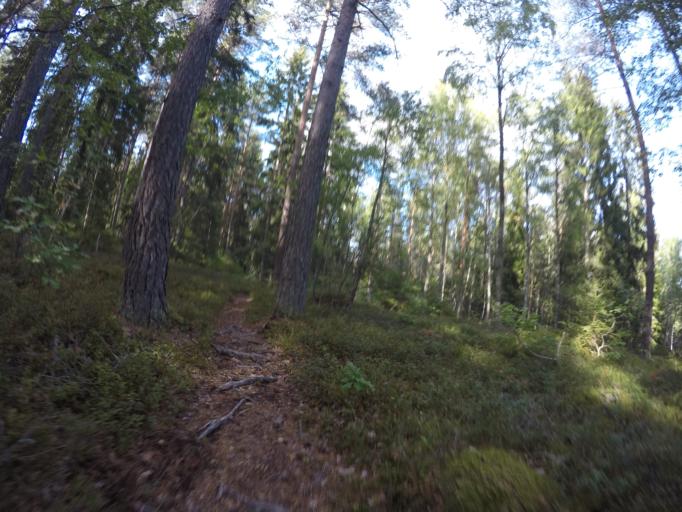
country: SE
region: Soedermanland
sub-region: Eskilstuna Kommun
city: Kvicksund
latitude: 59.5298
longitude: 16.3323
